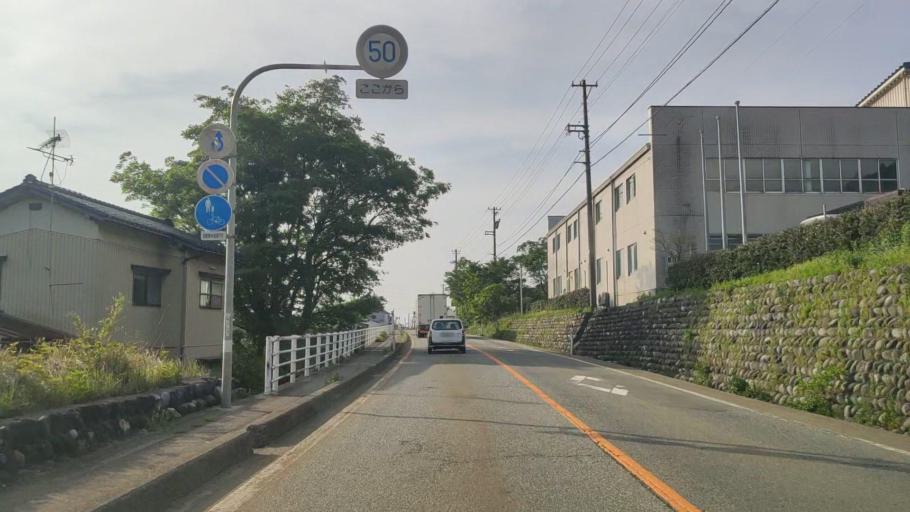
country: JP
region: Toyama
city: Yatsuomachi-higashikumisaka
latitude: 36.5611
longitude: 137.2147
